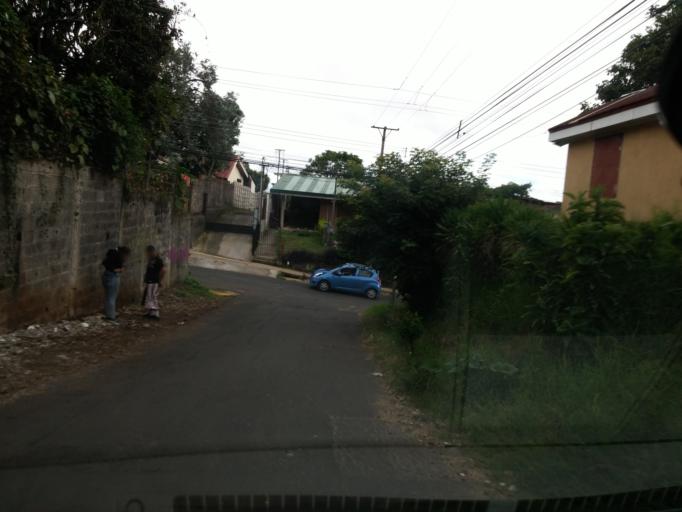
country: CR
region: Heredia
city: San Josecito
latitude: 10.0198
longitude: -84.1037
